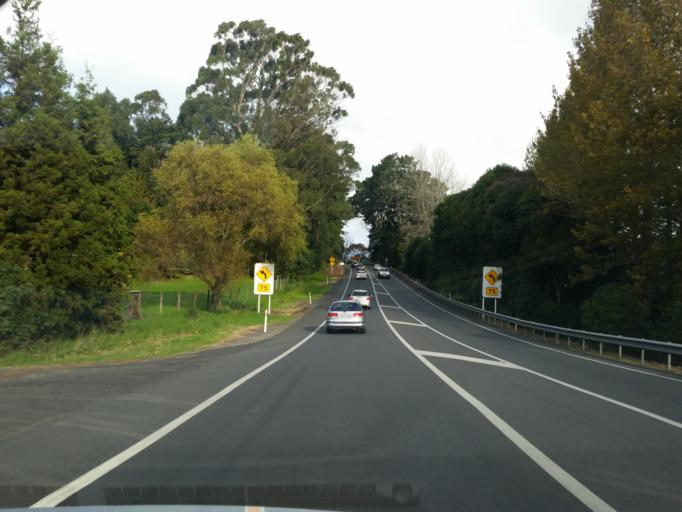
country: NZ
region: Bay of Plenty
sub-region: Tauranga City
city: Tauranga
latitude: -37.6978
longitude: 176.0770
